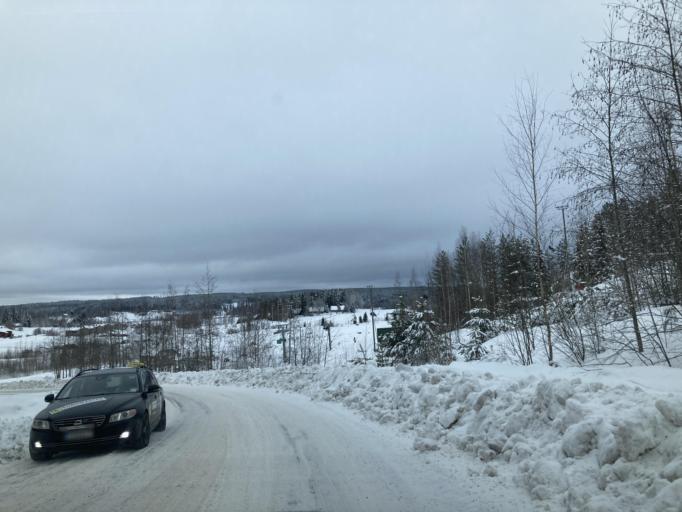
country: FI
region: Central Finland
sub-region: Jaemsae
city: Jaemsae
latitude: 61.8800
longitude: 25.3065
